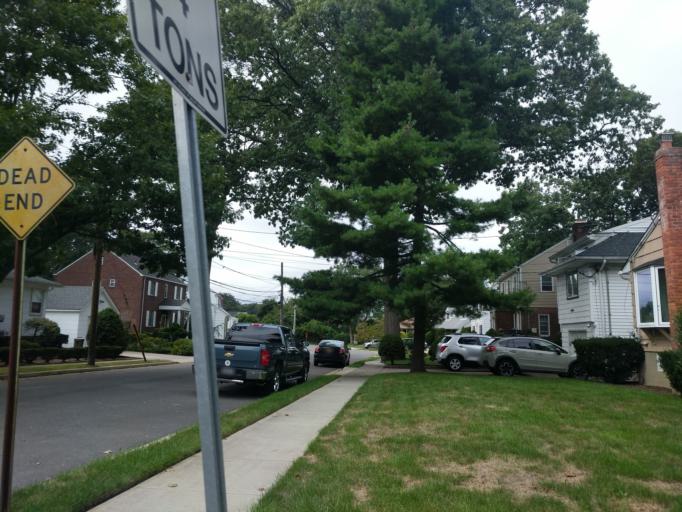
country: US
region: New York
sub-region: Nassau County
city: Malverne
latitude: 40.6693
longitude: -73.6851
